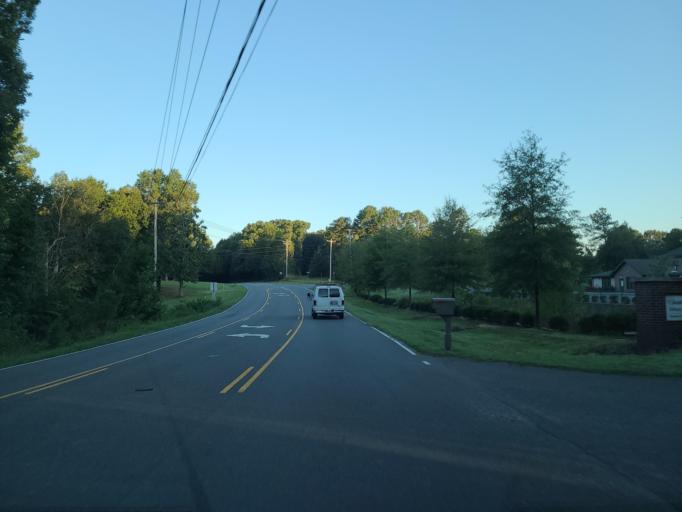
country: US
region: North Carolina
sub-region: Union County
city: Weddington
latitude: 35.0113
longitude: -80.7413
